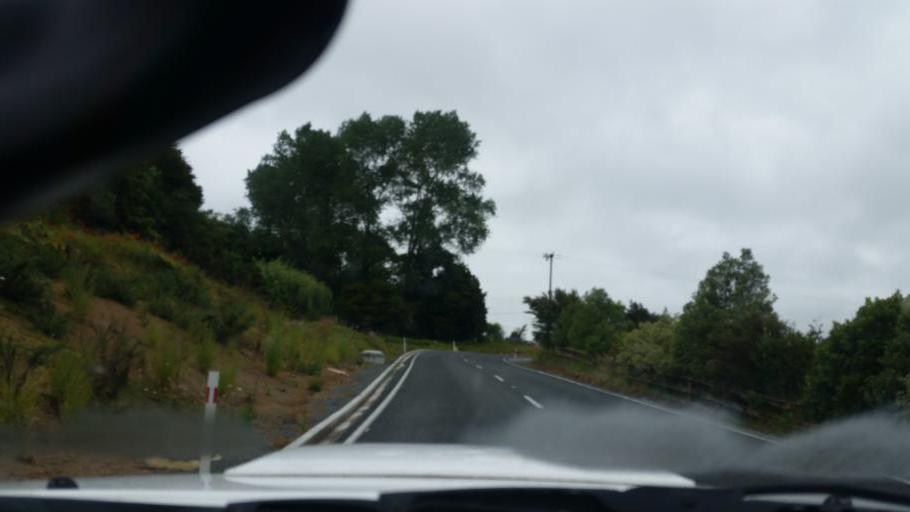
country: NZ
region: Auckland
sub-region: Auckland
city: Wellsford
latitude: -36.1719
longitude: 174.4586
